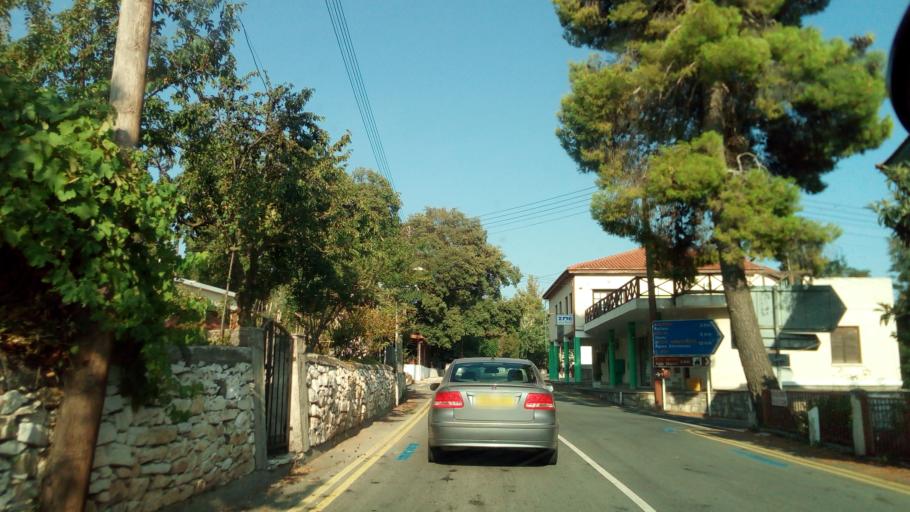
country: CY
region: Limassol
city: Pelendri
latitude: 34.8598
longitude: 32.8746
